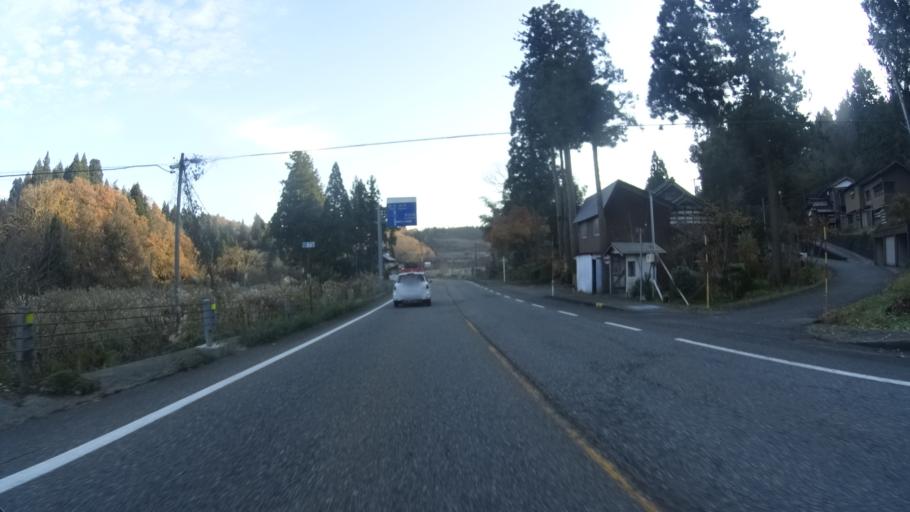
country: JP
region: Niigata
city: Kashiwazaki
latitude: 37.4092
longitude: 138.6863
